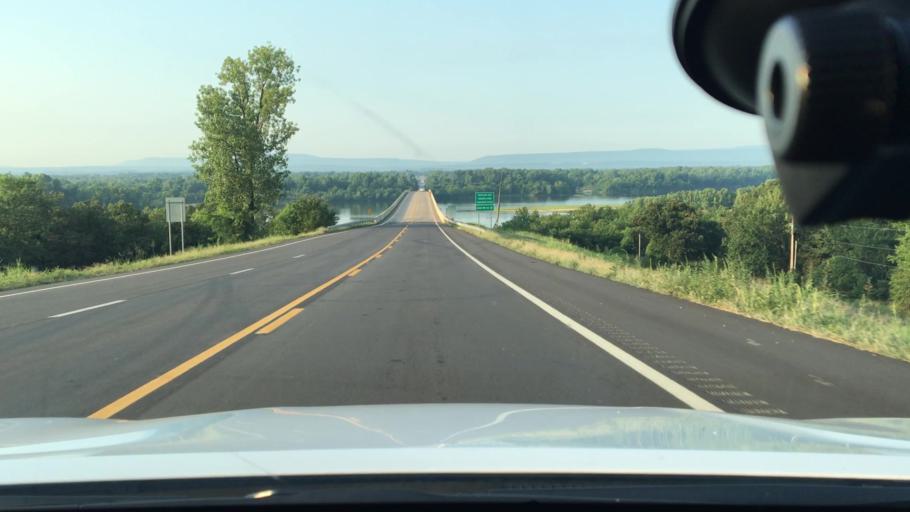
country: US
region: Arkansas
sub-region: Johnson County
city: Clarksville
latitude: 35.4147
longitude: -93.5324
